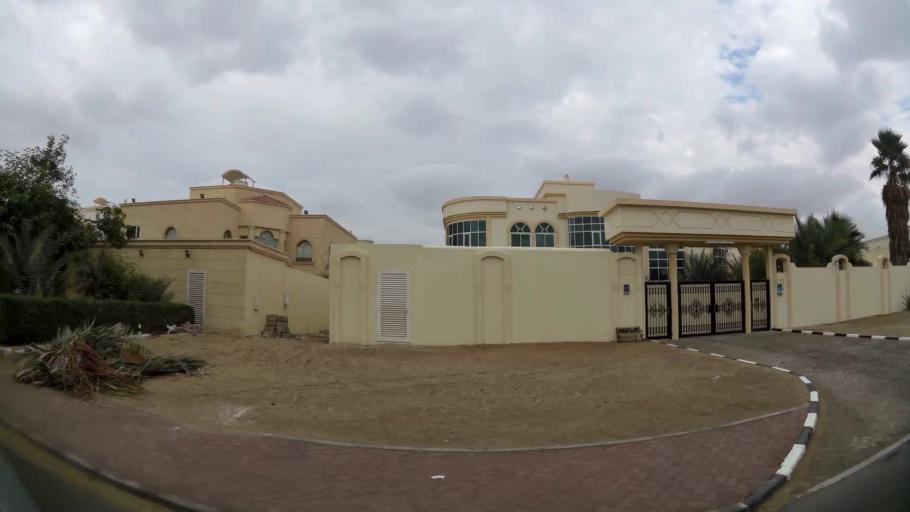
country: AE
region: Abu Dhabi
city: Abu Dhabi
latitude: 24.3536
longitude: 54.6297
